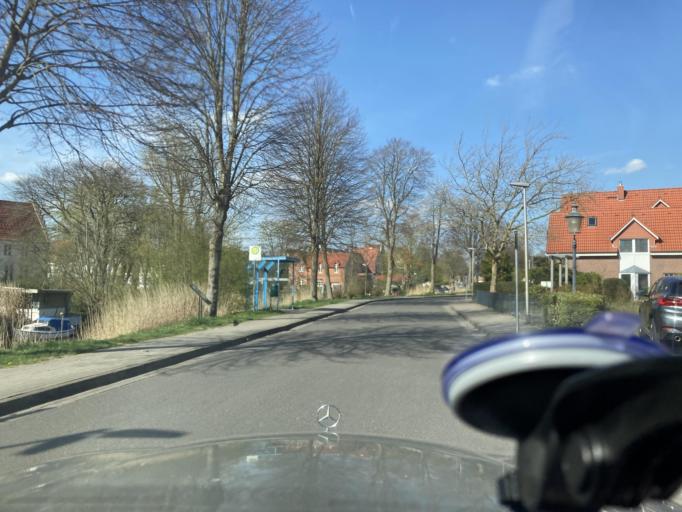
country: DE
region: Schleswig-Holstein
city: Friedrichstadt
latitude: 54.3753
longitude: 9.0914
